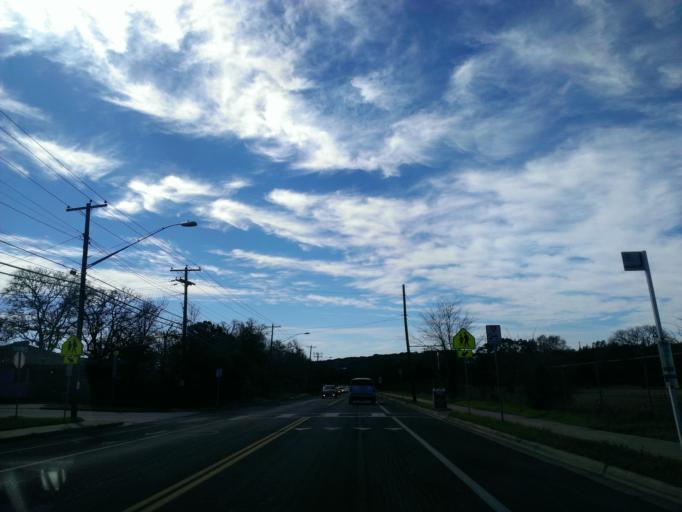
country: US
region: Texas
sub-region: Travis County
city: Rollingwood
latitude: 30.2862
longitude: -97.7750
